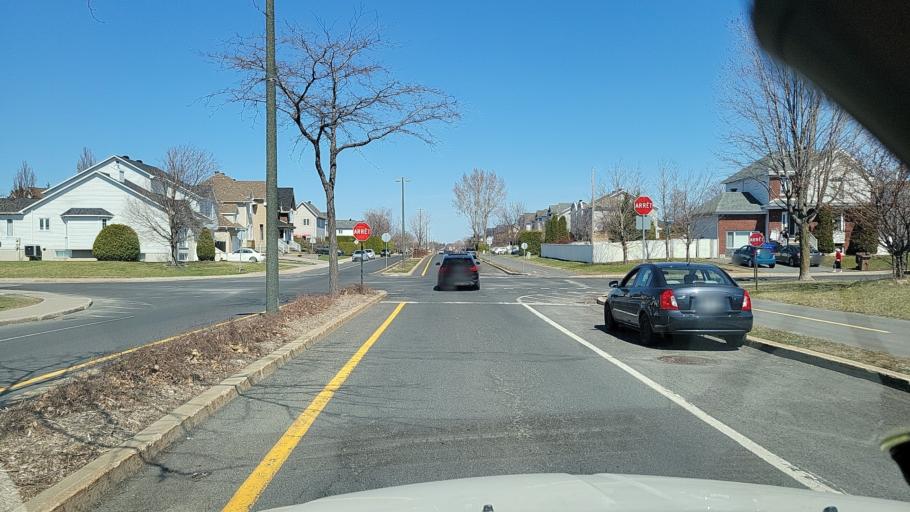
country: CA
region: Quebec
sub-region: Monteregie
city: Sainte-Julie
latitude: 45.5812
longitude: -73.3446
